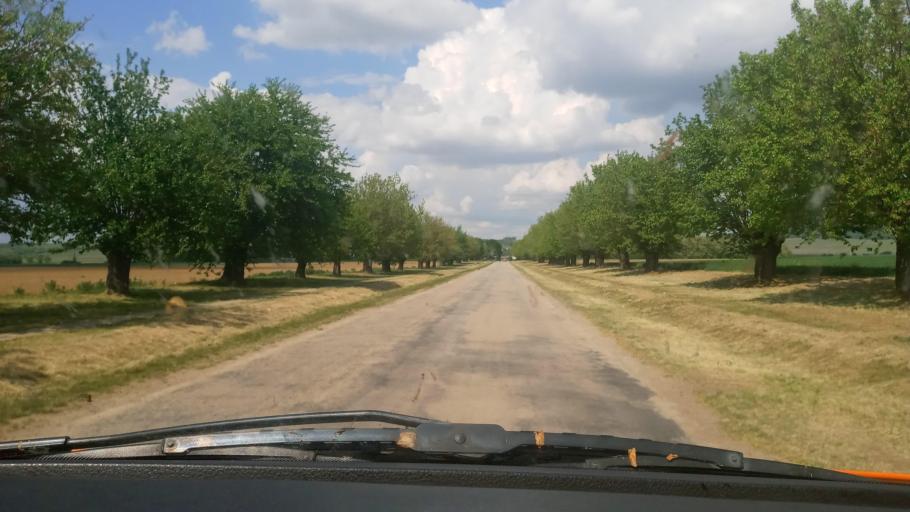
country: HU
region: Baranya
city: Siklos
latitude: 45.8510
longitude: 18.3582
